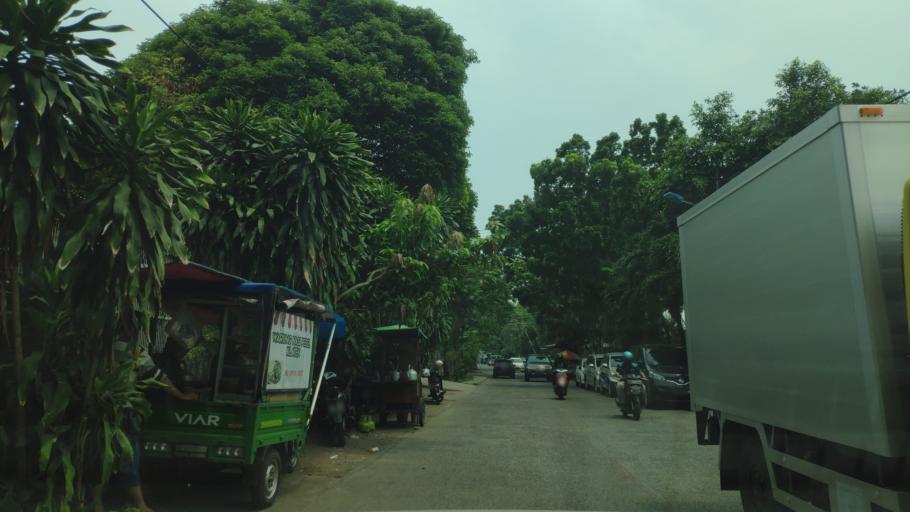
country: ID
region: Jakarta Raya
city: Jakarta
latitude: -6.1908
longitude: 106.8052
